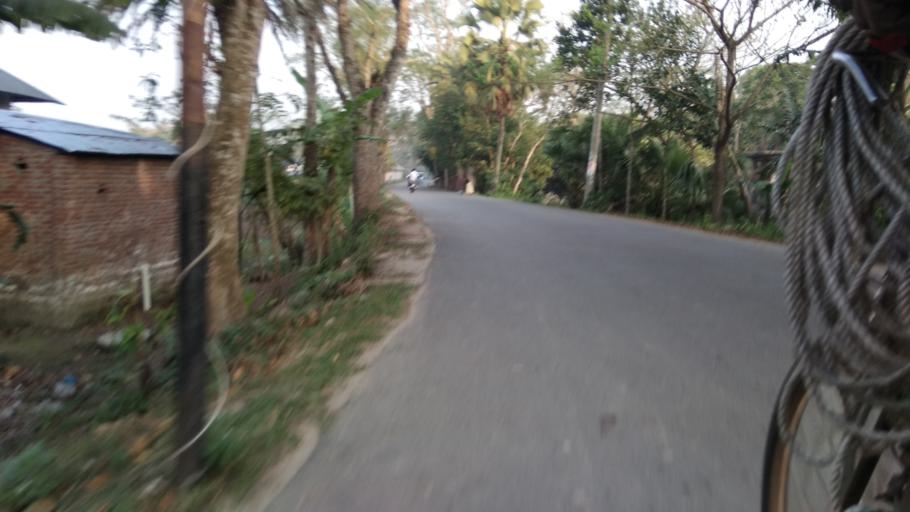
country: BD
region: Barisal
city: Mehendiganj
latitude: 22.9206
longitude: 90.4088
